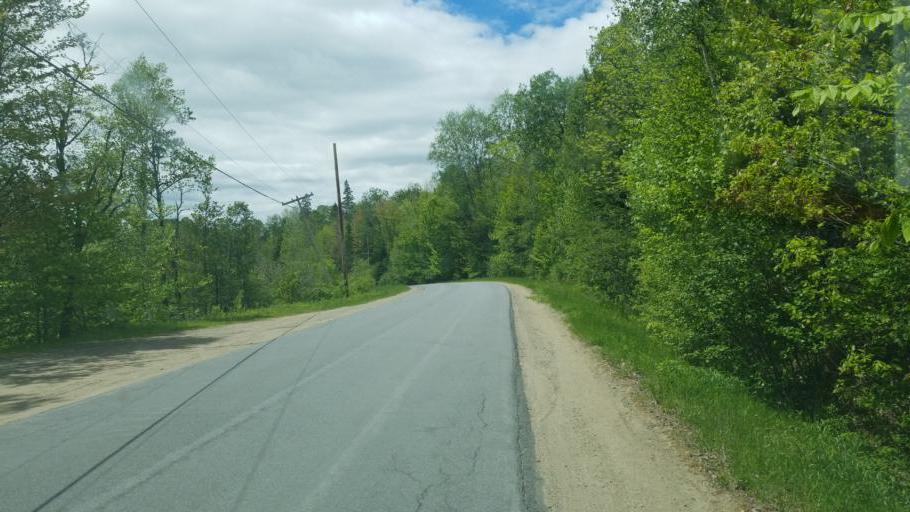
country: US
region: New York
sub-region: Hamilton County
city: Lake Pleasant
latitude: 43.7843
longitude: -74.3179
